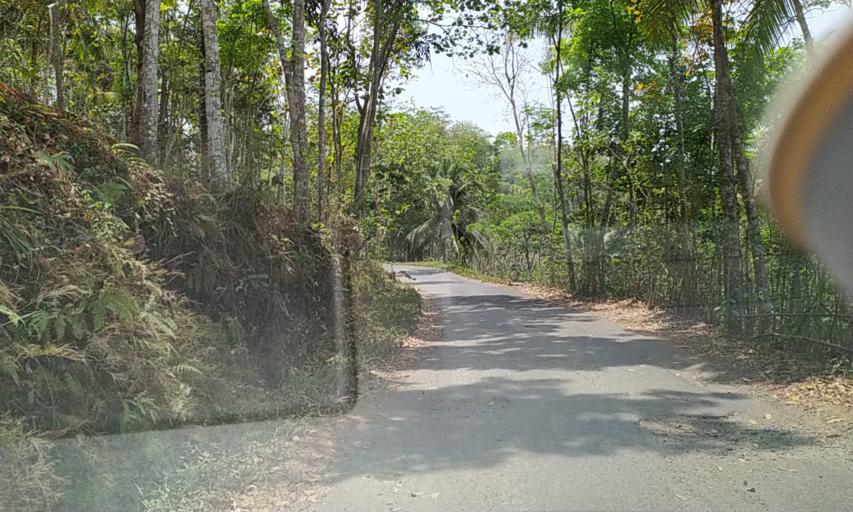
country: ID
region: Central Java
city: Pasanggrahan
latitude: -7.3658
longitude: 108.9003
